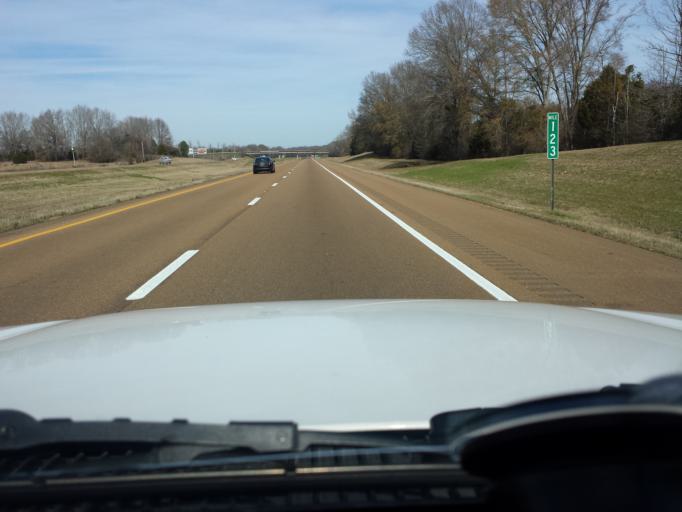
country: US
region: Mississippi
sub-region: Madison County
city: Canton
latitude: 32.6635
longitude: -90.0612
